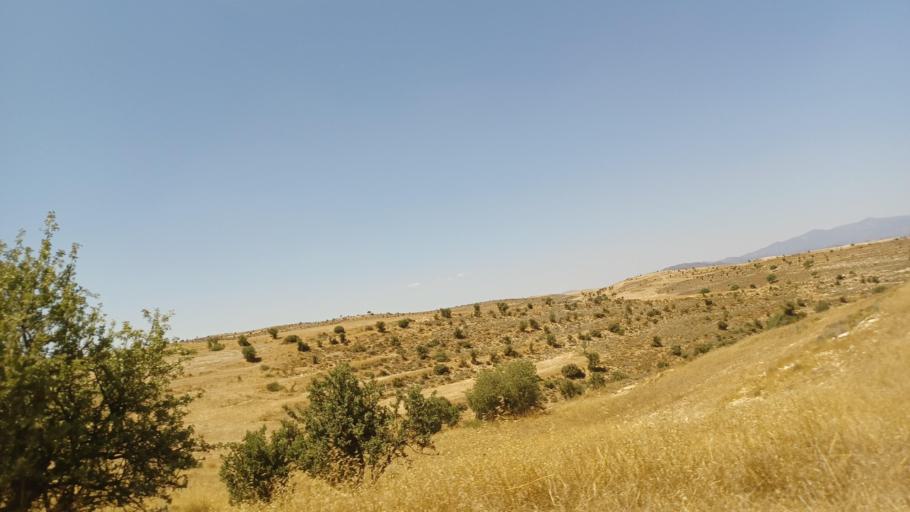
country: CY
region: Lefkosia
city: Lympia
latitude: 34.9829
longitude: 33.4833
